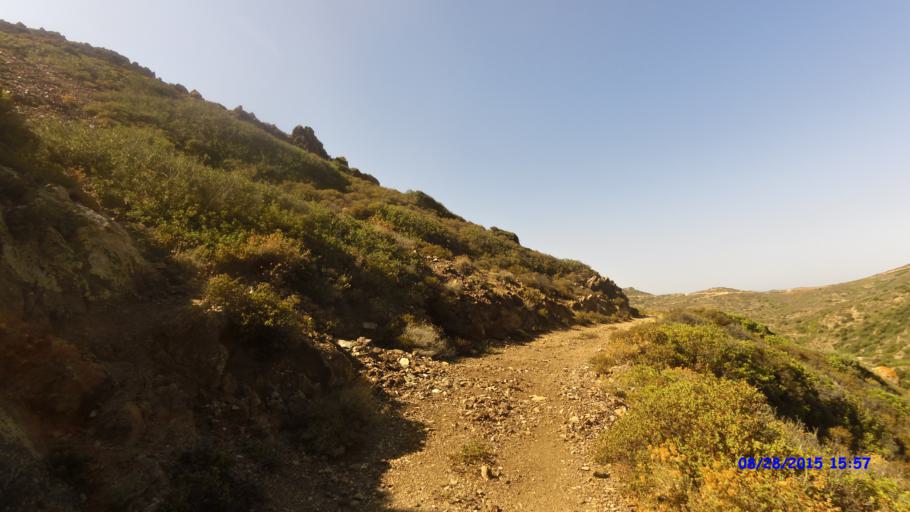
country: GR
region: South Aegean
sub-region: Nomos Kykladon
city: Antiparos
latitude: 36.9982
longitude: 25.0386
